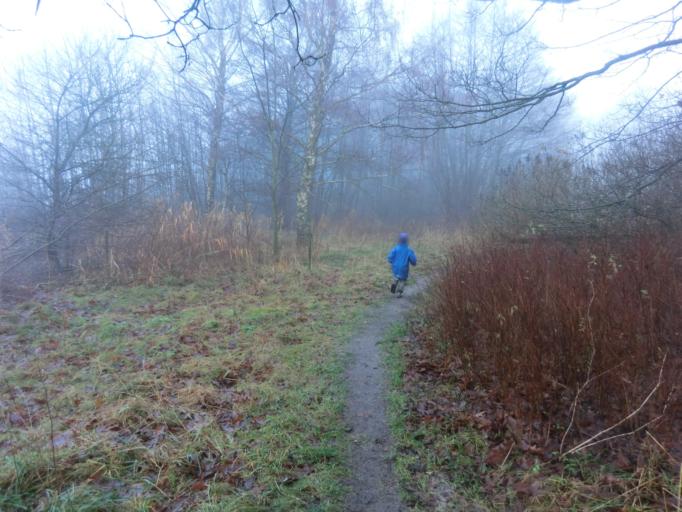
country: SE
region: Skane
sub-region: Lunds Kommun
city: Veberod
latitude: 55.6901
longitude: 13.4935
